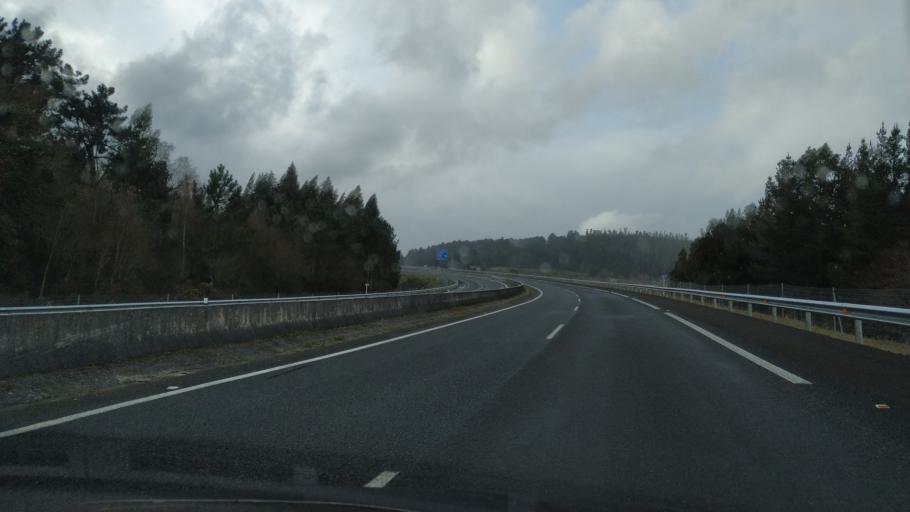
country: ES
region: Galicia
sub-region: Provincia de Pontevedra
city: Silleda
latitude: 42.7282
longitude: -8.3255
